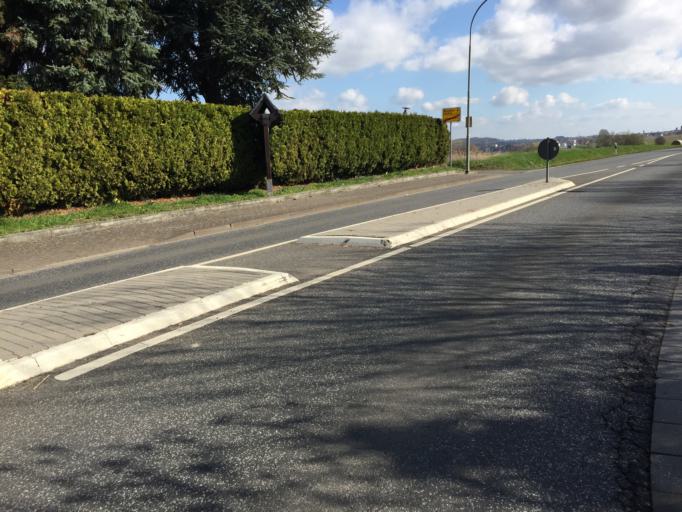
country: DE
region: Hesse
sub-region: Regierungsbezirk Giessen
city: Langgons
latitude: 50.5295
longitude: 8.6840
